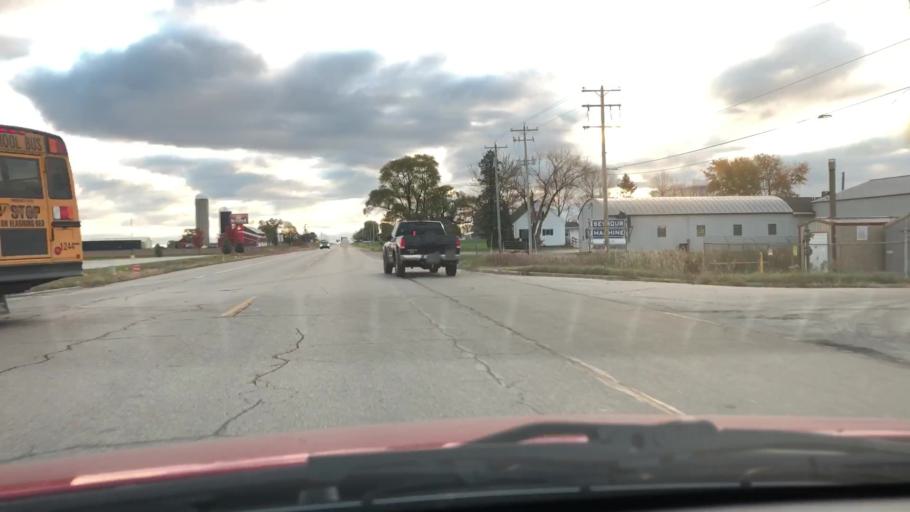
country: US
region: Wisconsin
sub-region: Outagamie County
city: Seymour
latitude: 44.5005
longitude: -88.3207
